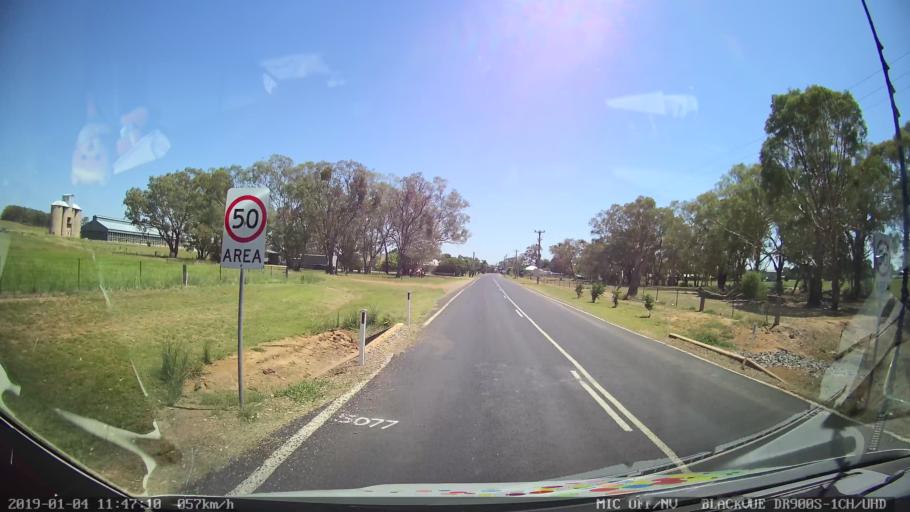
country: AU
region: New South Wales
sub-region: Cabonne
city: Molong
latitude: -32.9348
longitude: 148.7554
